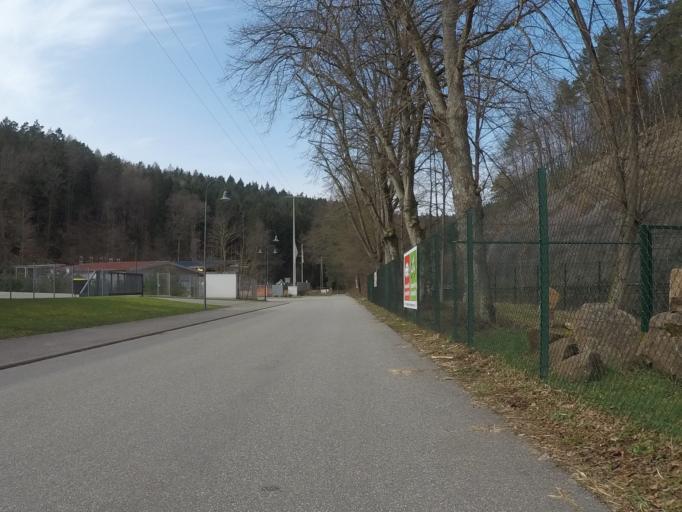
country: DE
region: Rheinland-Pfalz
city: Hauenstein
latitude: 49.2012
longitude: 7.8182
